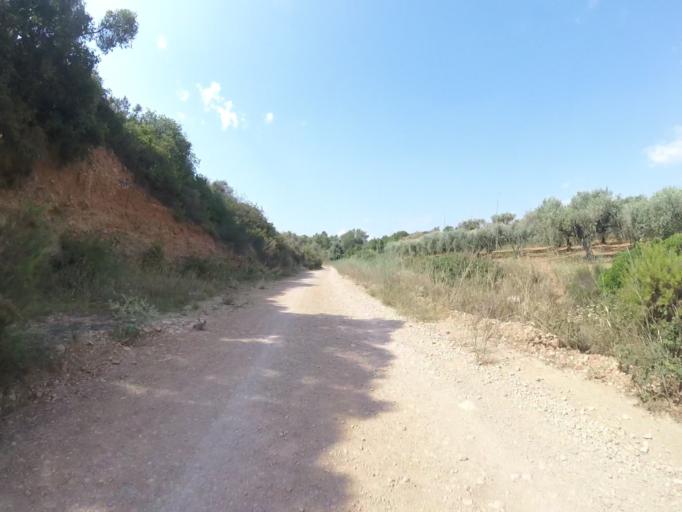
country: ES
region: Valencia
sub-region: Provincia de Castello
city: Cuevas de Vinroma
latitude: 40.3054
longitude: 0.1702
